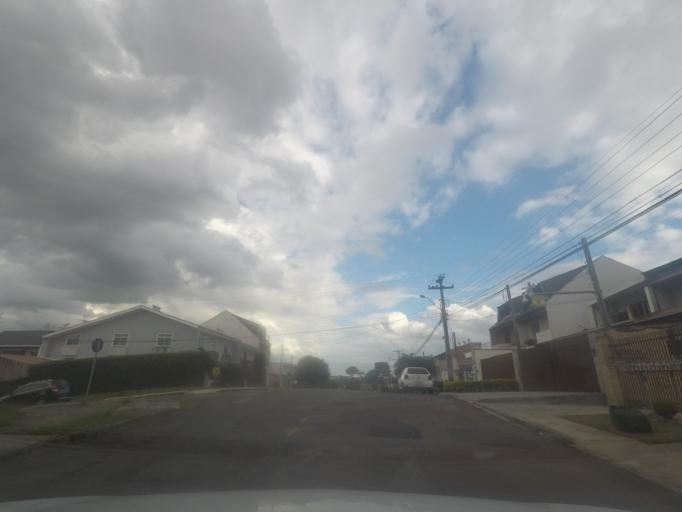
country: BR
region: Parana
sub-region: Pinhais
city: Pinhais
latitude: -25.4658
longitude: -49.2212
